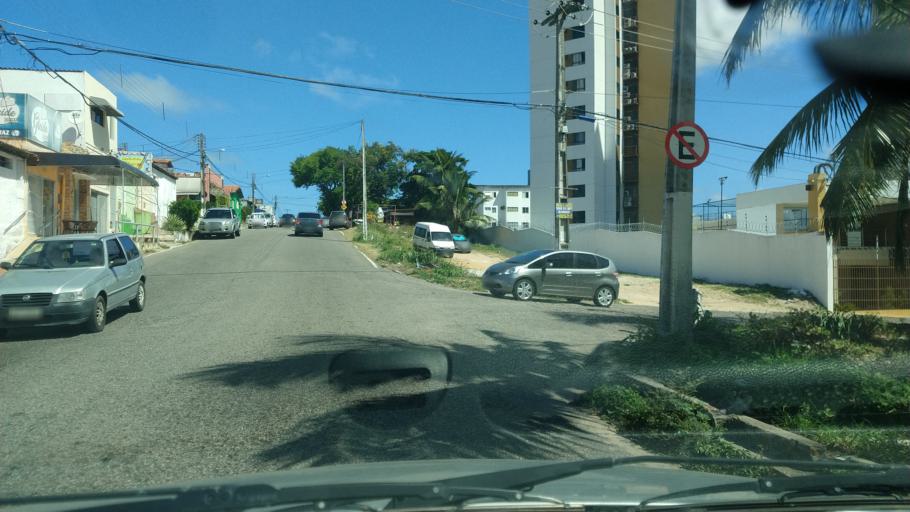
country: BR
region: Rio Grande do Norte
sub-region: Natal
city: Natal
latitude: -5.8584
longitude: -35.2092
